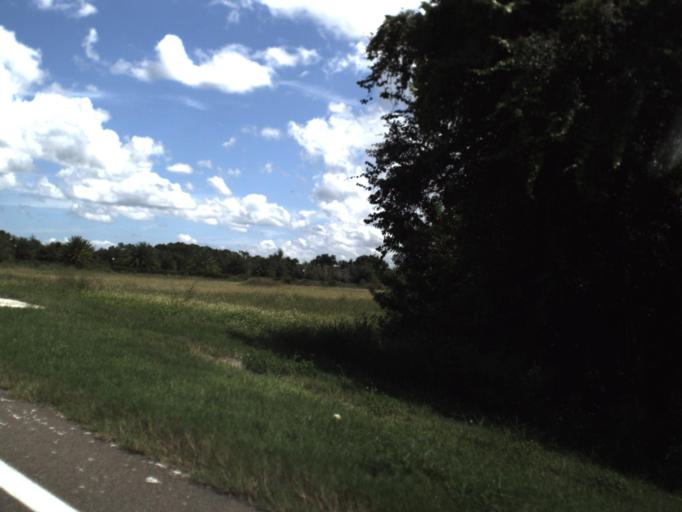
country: US
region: Florida
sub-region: Polk County
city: Lake Alfred
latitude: 28.0683
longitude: -81.6795
